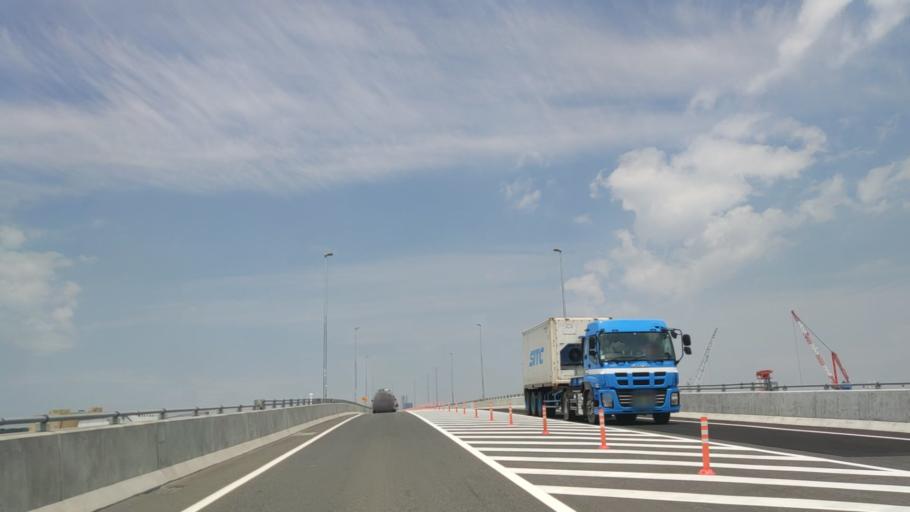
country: JP
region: Kanagawa
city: Yokohama
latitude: 35.4106
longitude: 139.6826
